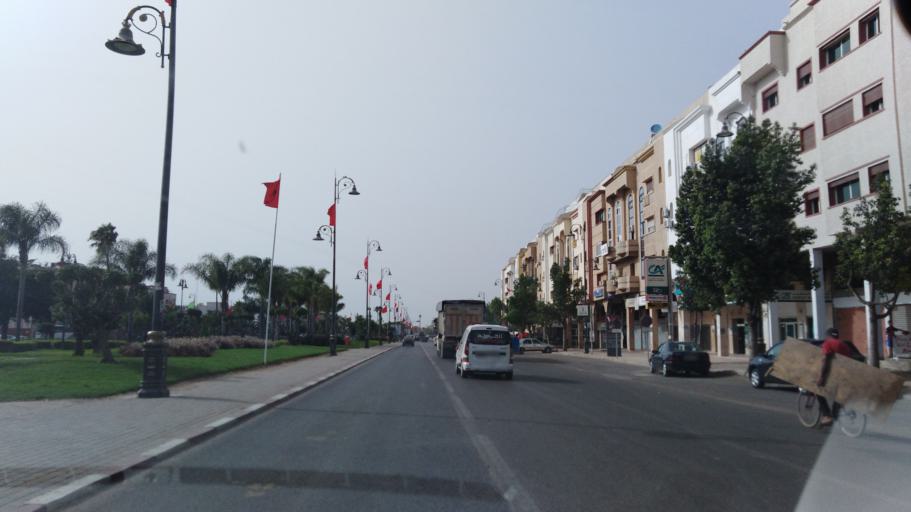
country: MA
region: Chaouia-Ouardigha
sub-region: Settat Province
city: Berrechid
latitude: 33.2632
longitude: -7.5816
